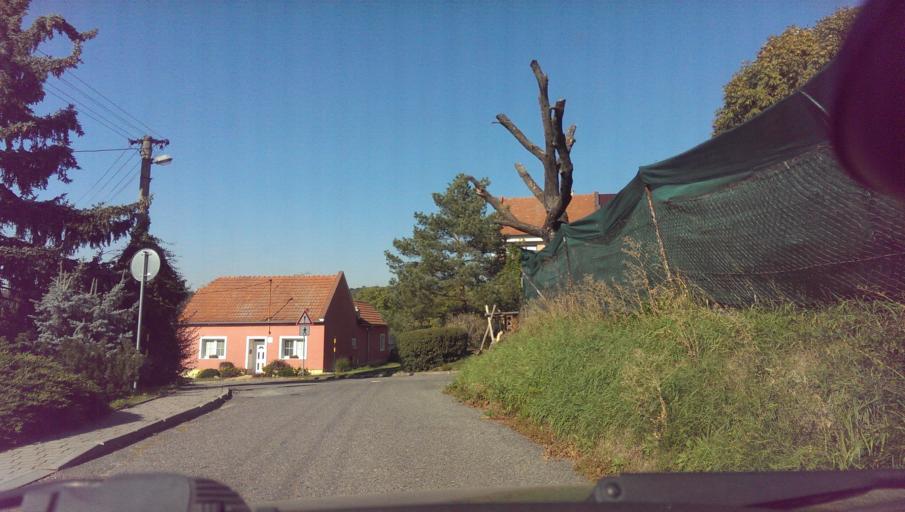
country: CZ
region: Zlin
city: Popovice
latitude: 49.0535
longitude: 17.5237
